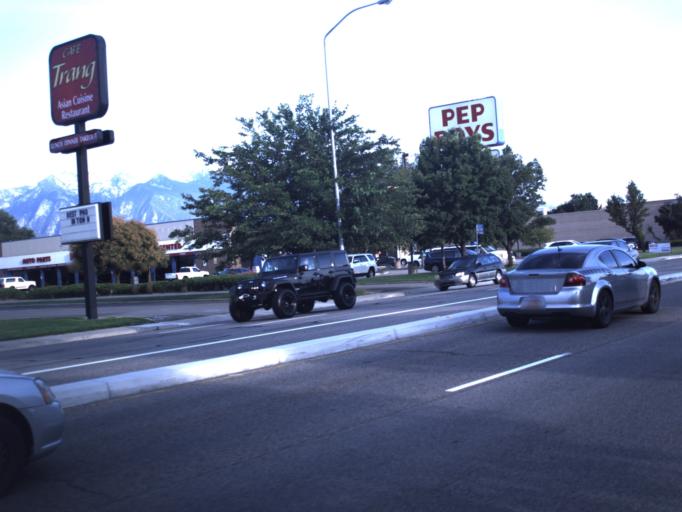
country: US
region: Utah
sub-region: Salt Lake County
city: Murray
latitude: 40.6405
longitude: -111.8892
